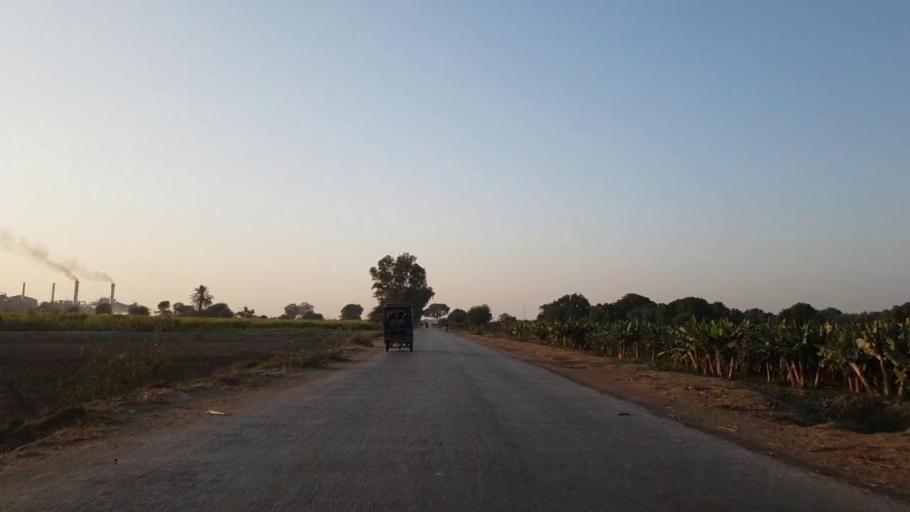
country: PK
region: Sindh
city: Chambar
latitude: 25.2484
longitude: 68.6798
